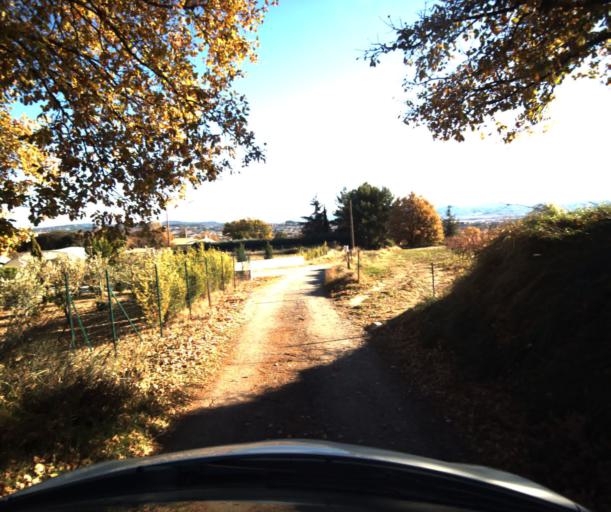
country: FR
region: Provence-Alpes-Cote d'Azur
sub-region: Departement du Vaucluse
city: Pertuis
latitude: 43.7101
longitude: 5.4844
